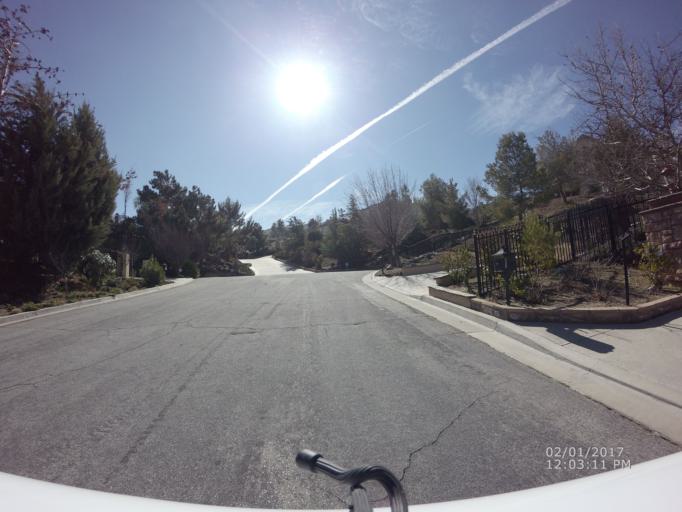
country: US
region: California
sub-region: Los Angeles County
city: Palmdale
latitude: 34.5453
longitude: -118.1372
